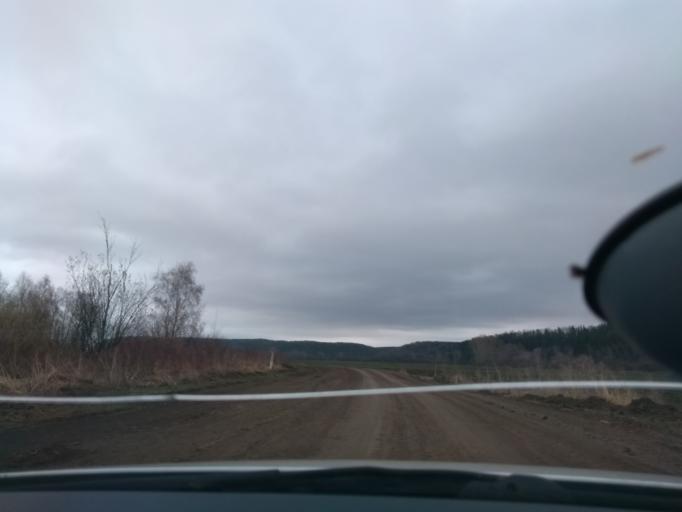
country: RU
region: Perm
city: Orda
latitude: 57.2489
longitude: 56.6170
